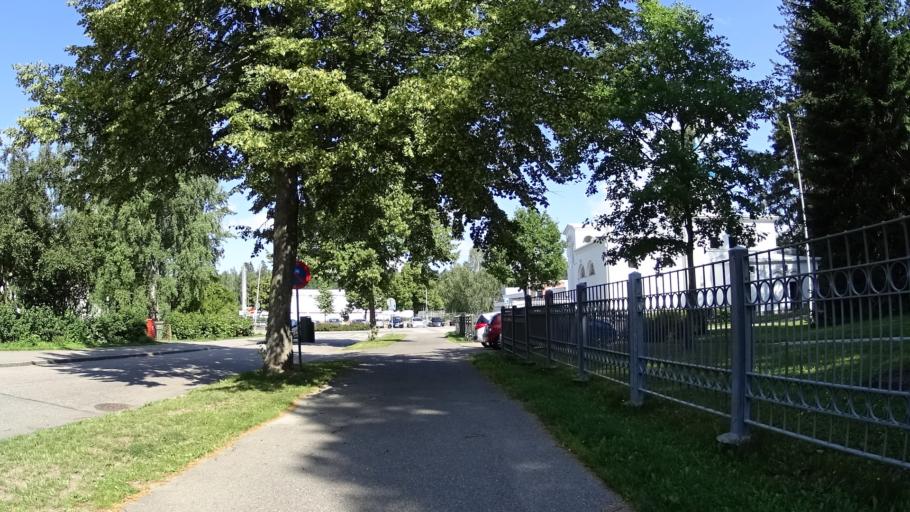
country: FI
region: Uusimaa
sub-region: Helsinki
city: Jaervenpaeae
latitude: 60.4800
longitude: 25.0923
